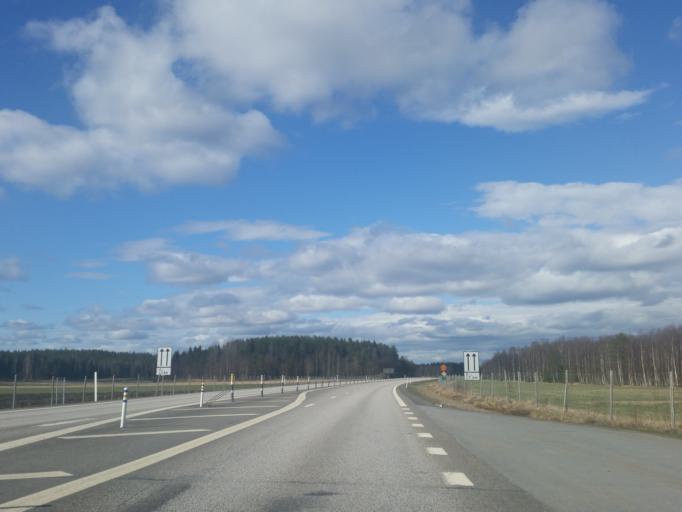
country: SE
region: Vaesterbotten
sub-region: Robertsfors Kommun
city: Robertsfors
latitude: 64.1393
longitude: 20.8946
